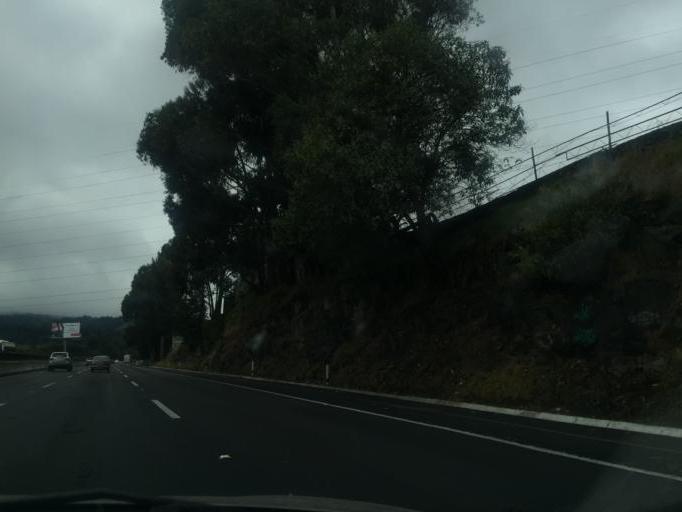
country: MX
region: Mexico City
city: Xochimilco
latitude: 19.1961
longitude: -99.1522
